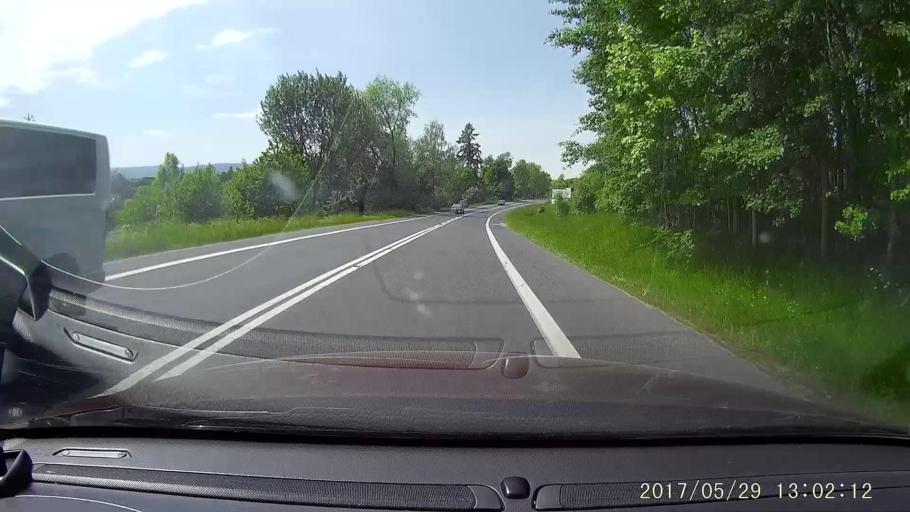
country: PL
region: Lower Silesian Voivodeship
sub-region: Powiat jeleniogorski
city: Stara Kamienica
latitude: 50.9130
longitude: 15.6321
